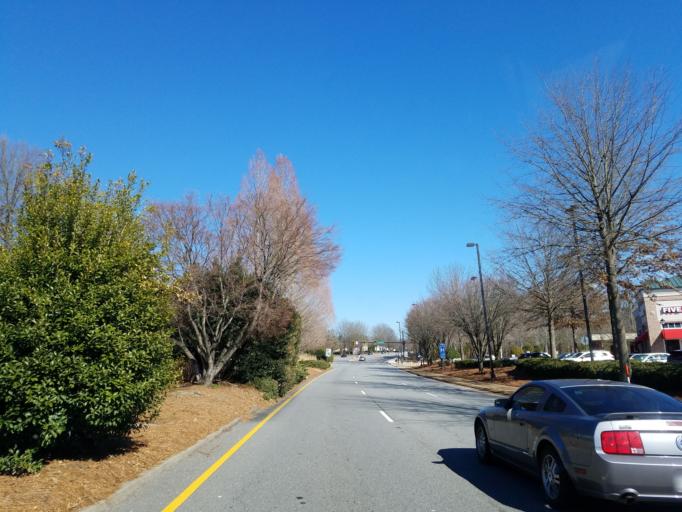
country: US
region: Georgia
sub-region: Fulton County
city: Alpharetta
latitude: 34.0434
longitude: -84.3012
